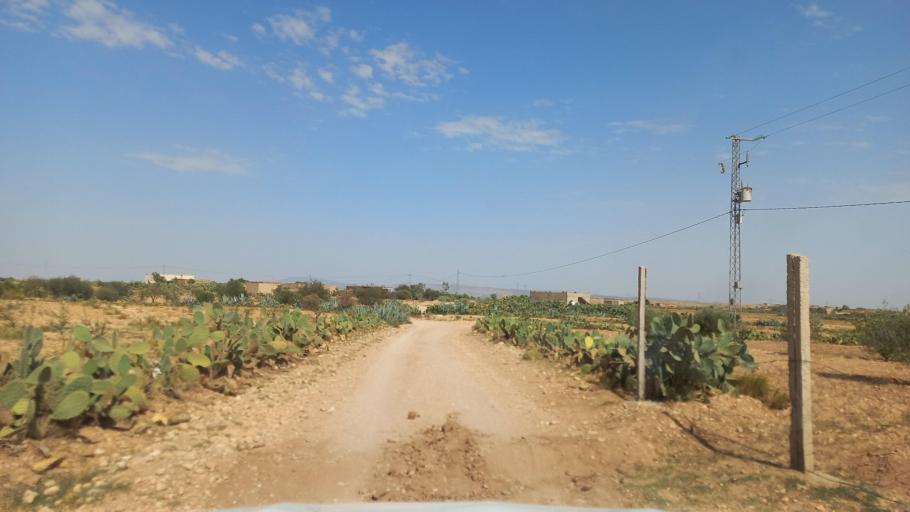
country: TN
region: Al Qasrayn
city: Kasserine
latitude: 35.2793
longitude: 8.9550
